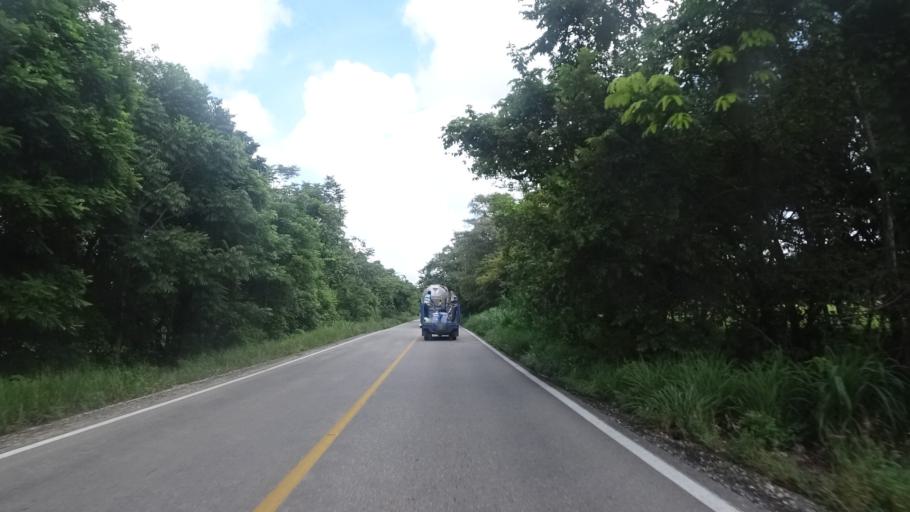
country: MX
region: Chiapas
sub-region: Catazaja
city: Catazaja
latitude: 17.6154
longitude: -92.0257
